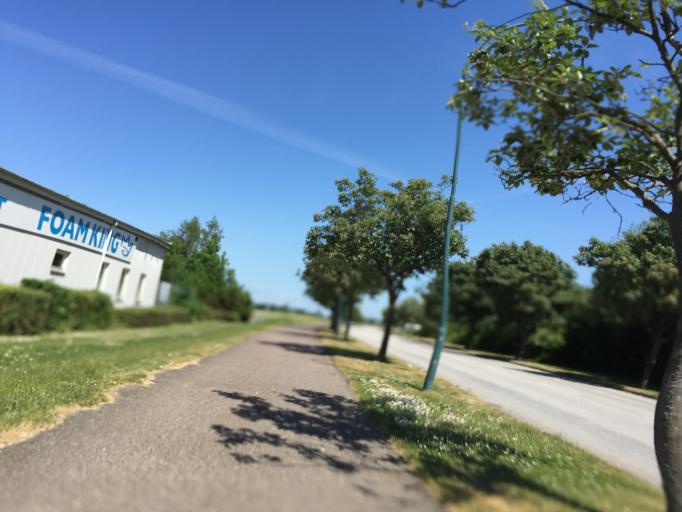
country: SE
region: Skane
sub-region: Trelleborgs Kommun
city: Trelleborg
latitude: 55.3807
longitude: 13.1243
